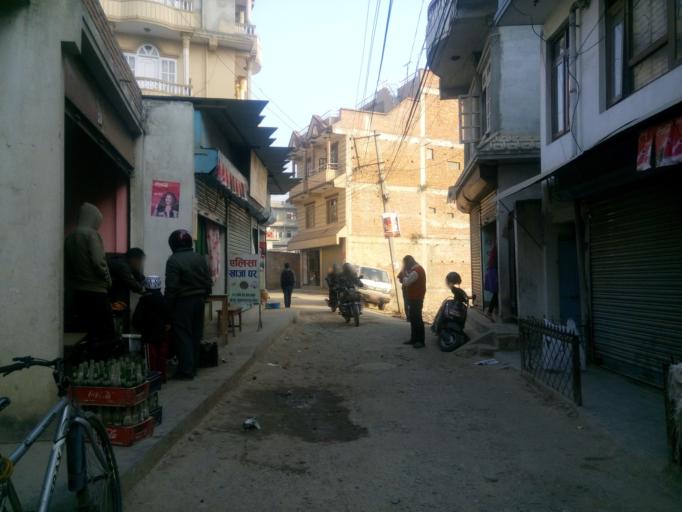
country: NP
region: Central Region
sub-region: Bagmati Zone
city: Patan
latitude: 27.6645
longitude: 85.3353
